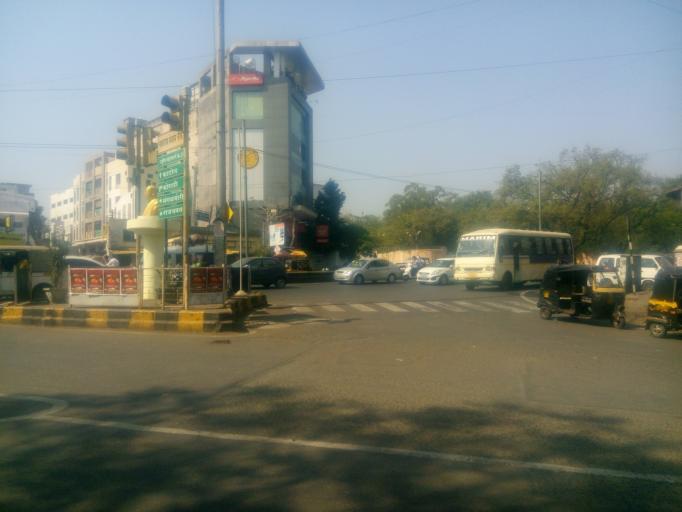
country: IN
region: Maharashtra
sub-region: Nagpur Division
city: Nagpur
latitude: 21.1635
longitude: 79.0798
